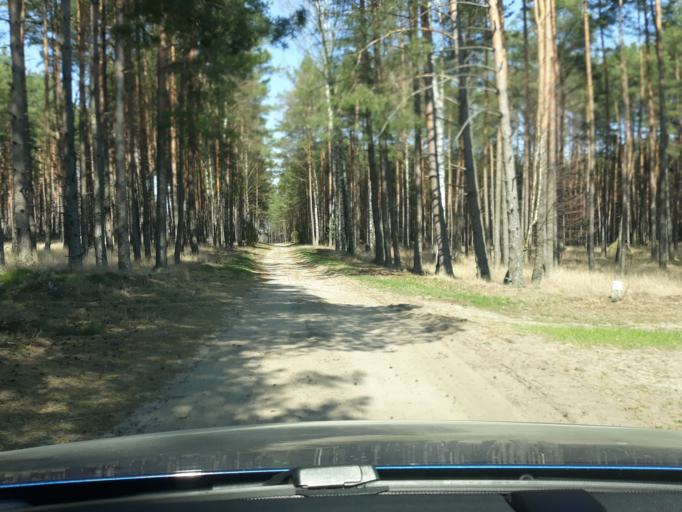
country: PL
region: Pomeranian Voivodeship
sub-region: Powiat bytowski
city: Lipnica
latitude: 53.8679
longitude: 17.4316
